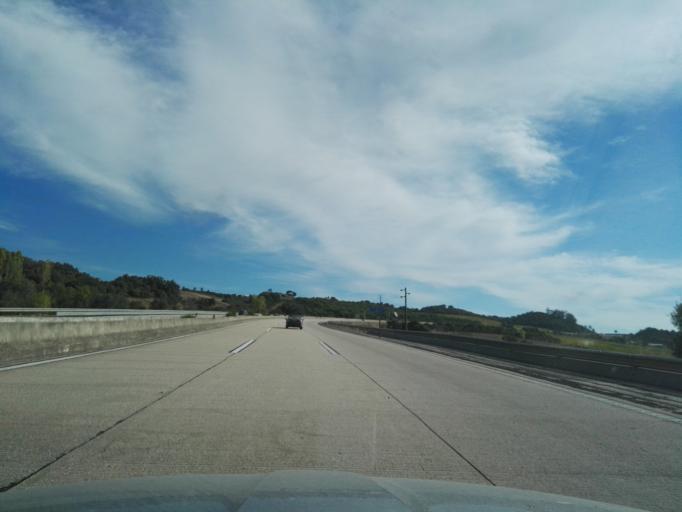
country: PT
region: Lisbon
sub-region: Loures
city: Bucelas
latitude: 38.9038
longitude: -9.0908
